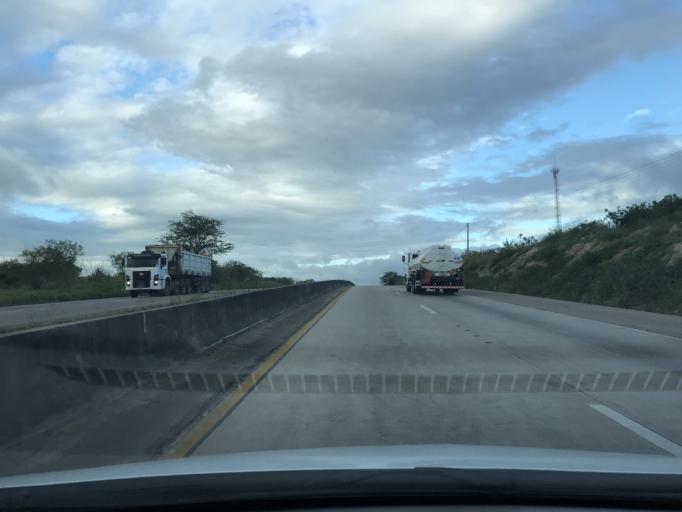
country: BR
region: Pernambuco
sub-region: Caruaru
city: Caruaru
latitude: -8.2990
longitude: -35.9046
